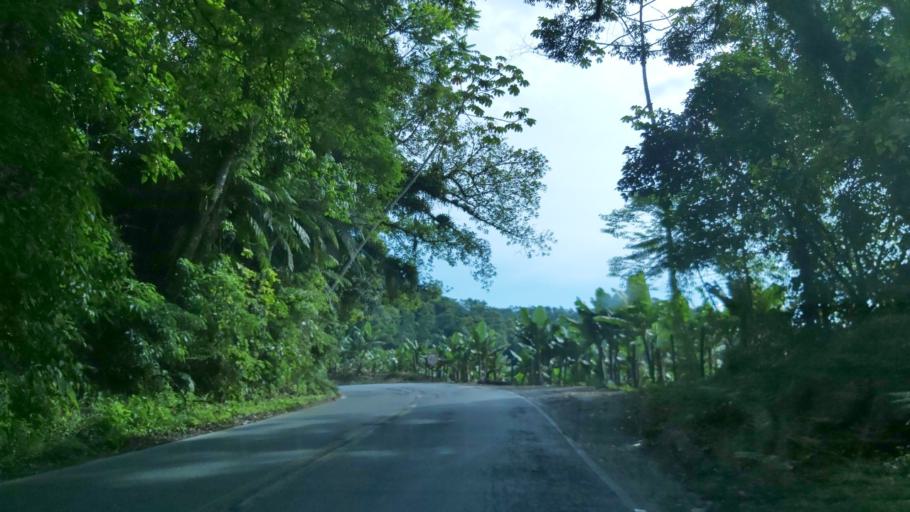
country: BR
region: Sao Paulo
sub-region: Juquia
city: Juquia
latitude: -24.0868
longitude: -47.6129
